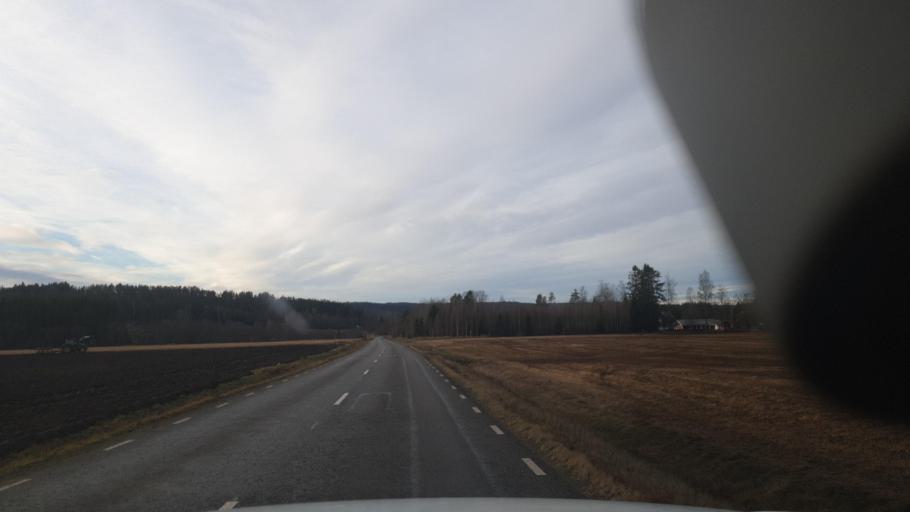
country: SE
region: Vaermland
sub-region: Eda Kommun
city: Amotfors
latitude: 59.6810
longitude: 12.1430
